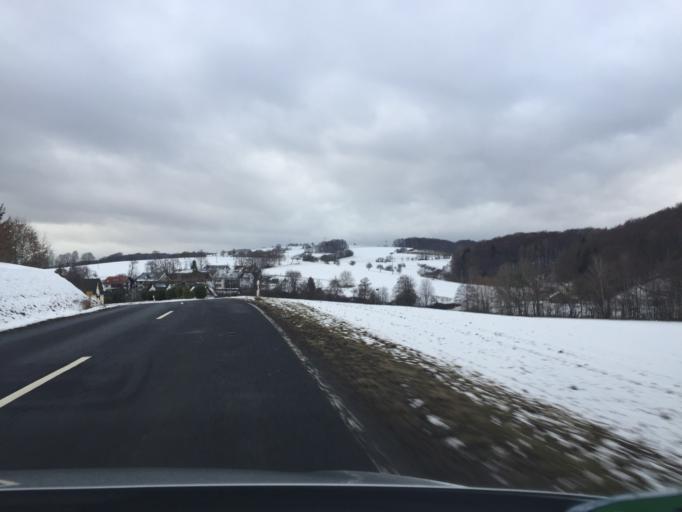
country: DE
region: Bavaria
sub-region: Regierungsbezirk Unterfranken
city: Krombach
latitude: 50.1058
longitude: 9.2224
